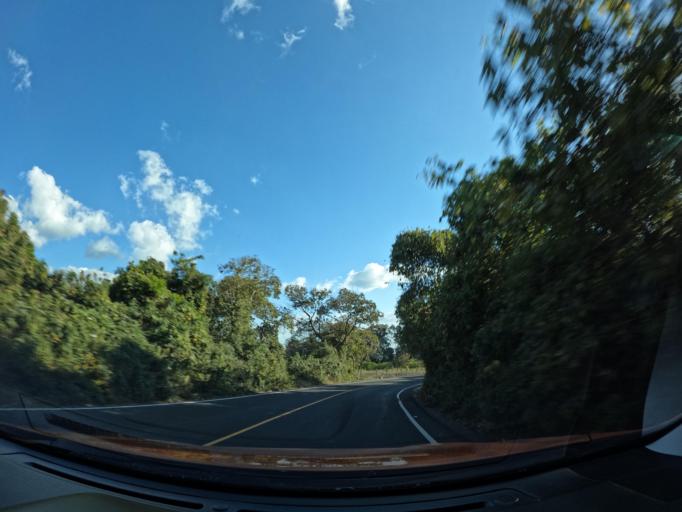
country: GT
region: Escuintla
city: Palin
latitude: 14.4533
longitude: -90.6941
